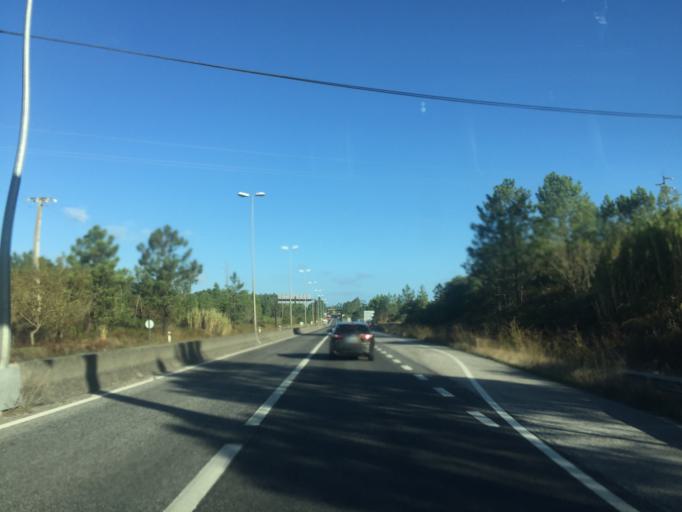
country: PT
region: Lisbon
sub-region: Azambuja
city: Alcoentre
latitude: 39.2330
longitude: -8.9549
